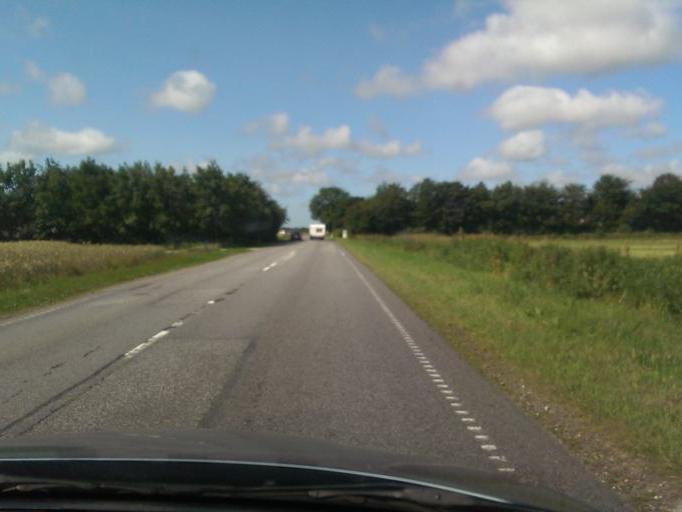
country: DK
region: North Denmark
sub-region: Bronderslev Kommune
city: Bronderslev
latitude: 57.2071
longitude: 9.8807
